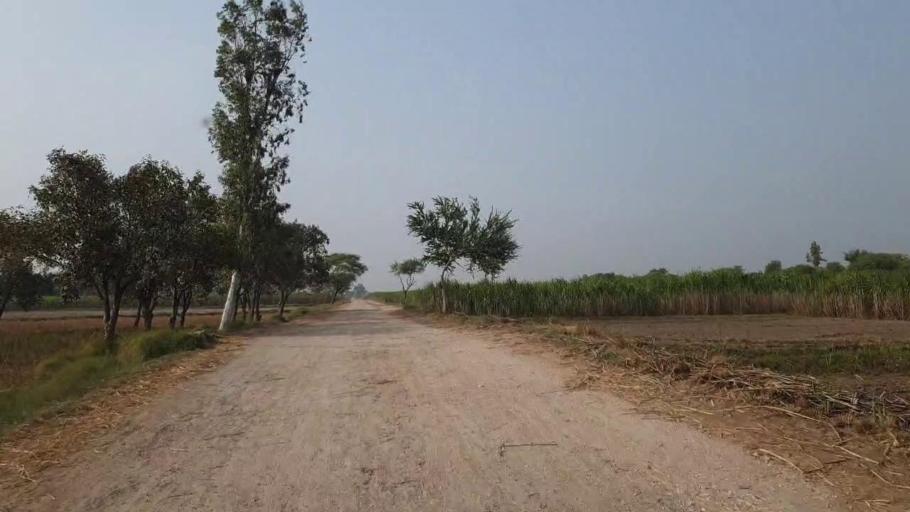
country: PK
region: Sindh
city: Matli
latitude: 25.0717
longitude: 68.5949
